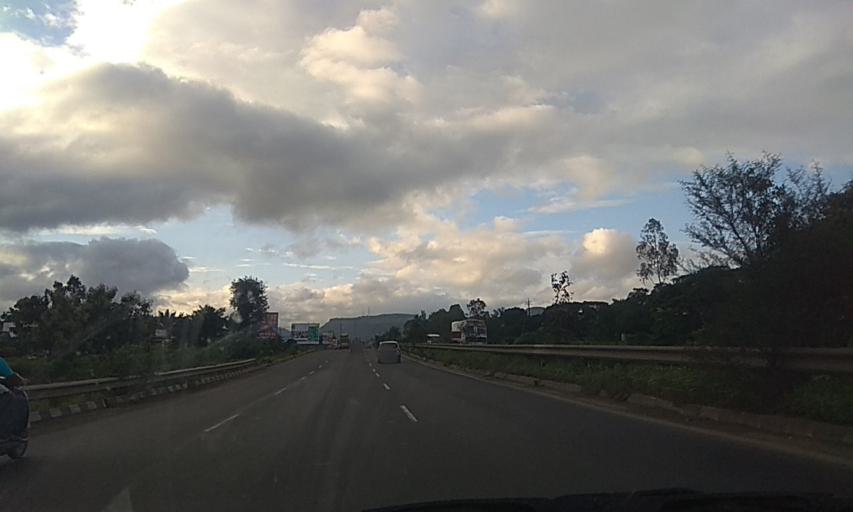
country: IN
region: Maharashtra
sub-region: Satara Division
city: Satara
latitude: 17.6200
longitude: 74.0195
